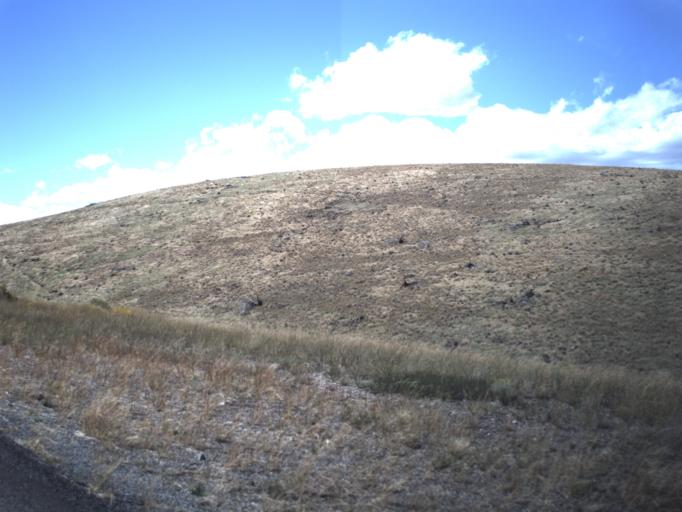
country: US
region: Utah
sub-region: Iron County
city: Parowan
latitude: 38.0889
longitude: -112.9534
